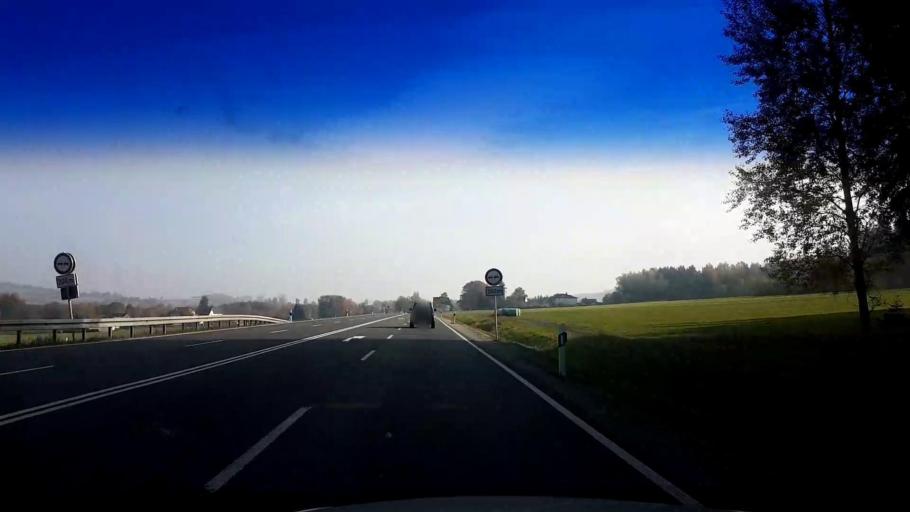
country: DE
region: Bavaria
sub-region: Upper Franconia
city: Trostau
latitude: 50.0167
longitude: 11.9278
